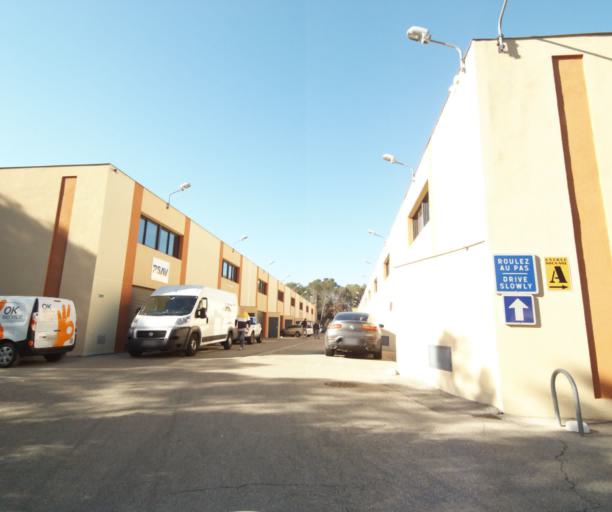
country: FR
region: Provence-Alpes-Cote d'Azur
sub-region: Departement des Alpes-Maritimes
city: Biot
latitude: 43.6095
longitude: 7.0713
